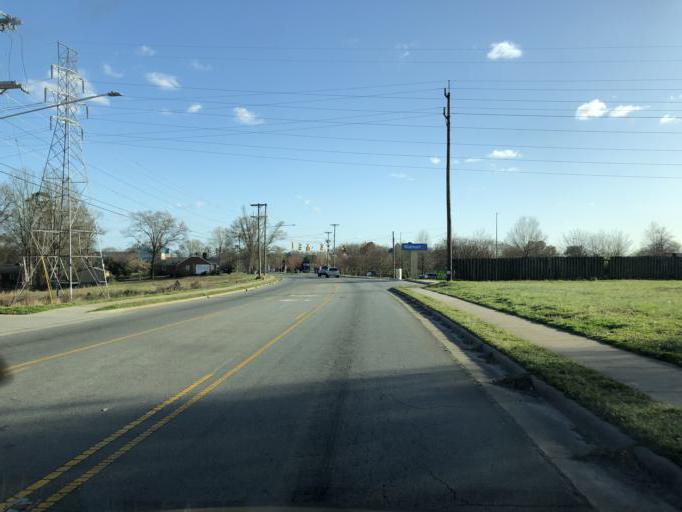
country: US
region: North Carolina
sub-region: Gaston County
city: Gastonia
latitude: 35.2624
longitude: -81.2231
